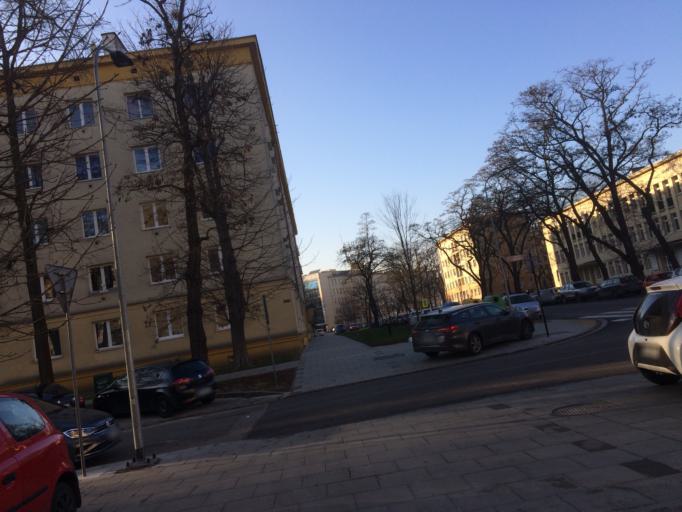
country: PL
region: Lesser Poland Voivodeship
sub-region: Powiat wielicki
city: Kokotow
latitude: 50.0768
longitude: 20.0372
